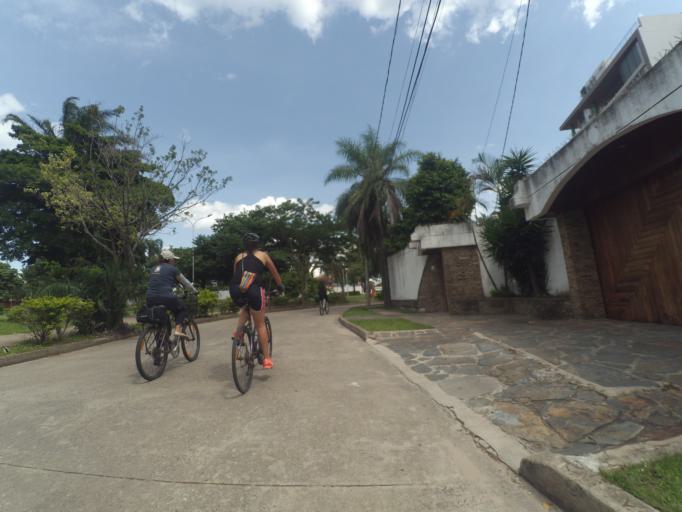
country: BO
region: Santa Cruz
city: Santa Cruz de la Sierra
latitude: -17.7655
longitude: -63.1735
